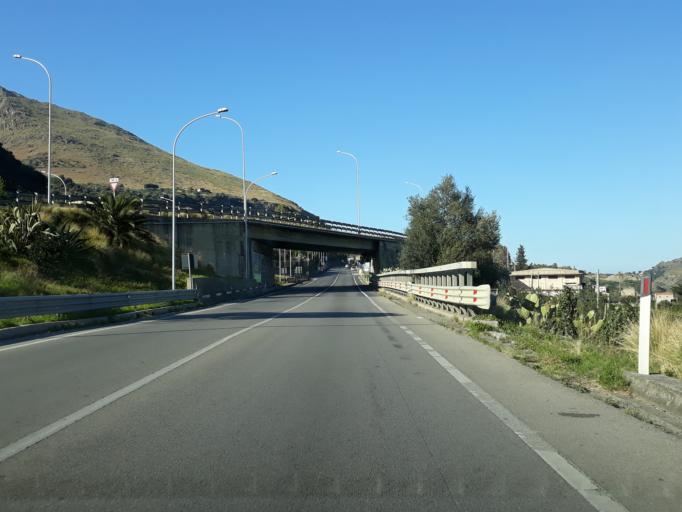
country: IT
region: Sicily
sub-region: Palermo
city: Misilmeri
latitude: 38.0426
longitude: 13.4608
